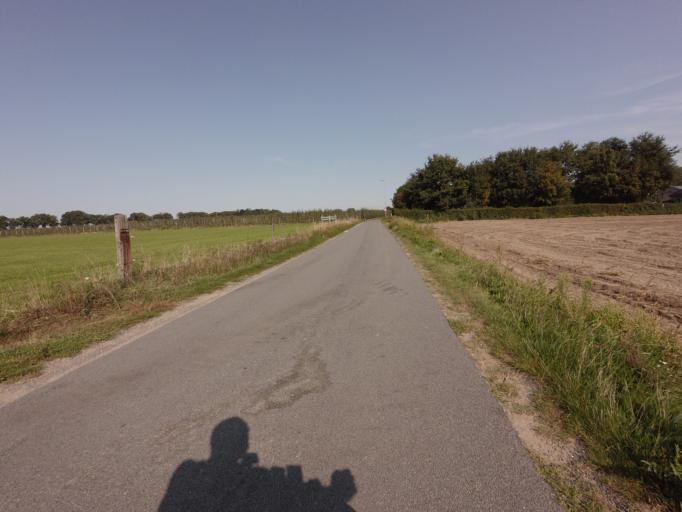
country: BE
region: Flanders
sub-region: Provincie Limburg
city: Maaseik
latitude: 51.1401
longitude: 5.8125
